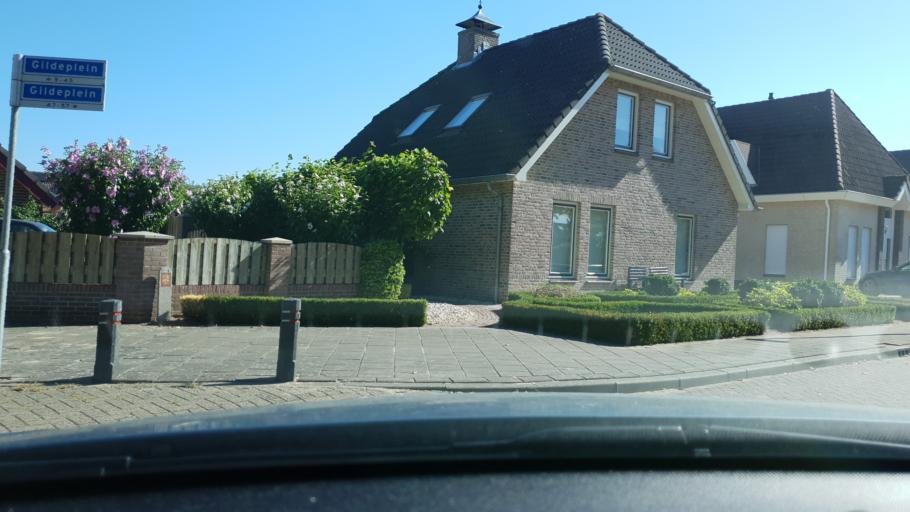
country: NL
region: North Brabant
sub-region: Gemeente Grave
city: Grave
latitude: 51.7726
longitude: 5.7455
